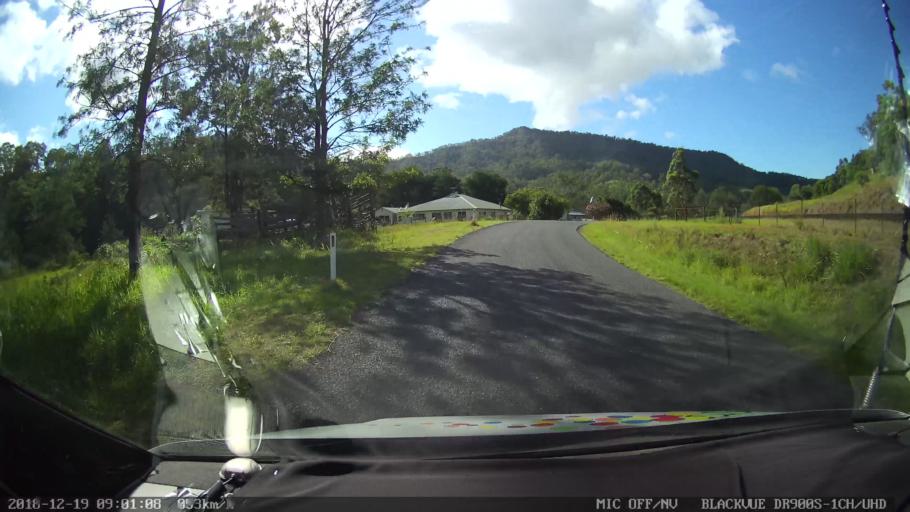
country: AU
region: New South Wales
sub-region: Kyogle
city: Kyogle
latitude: -28.4367
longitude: 152.9587
